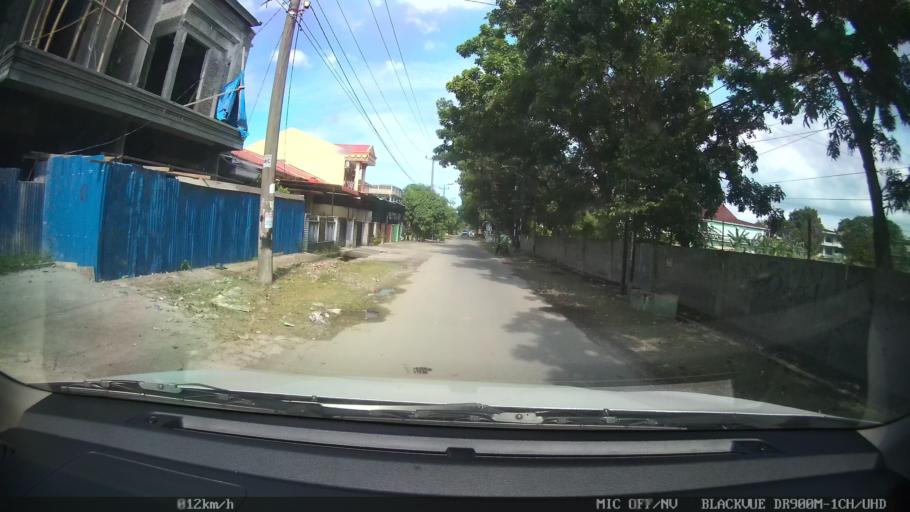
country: ID
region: North Sumatra
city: Medan
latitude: 3.6151
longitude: 98.6580
